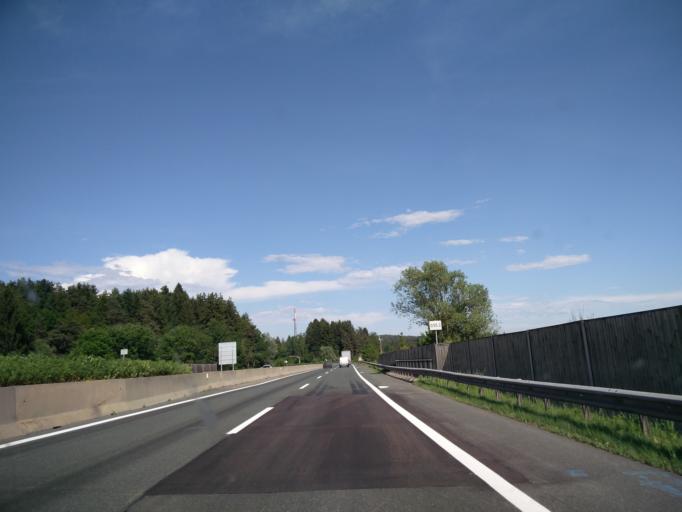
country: AT
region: Carinthia
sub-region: Politischer Bezirk Klagenfurt Land
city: Poggersdorf
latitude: 46.6446
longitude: 14.4970
